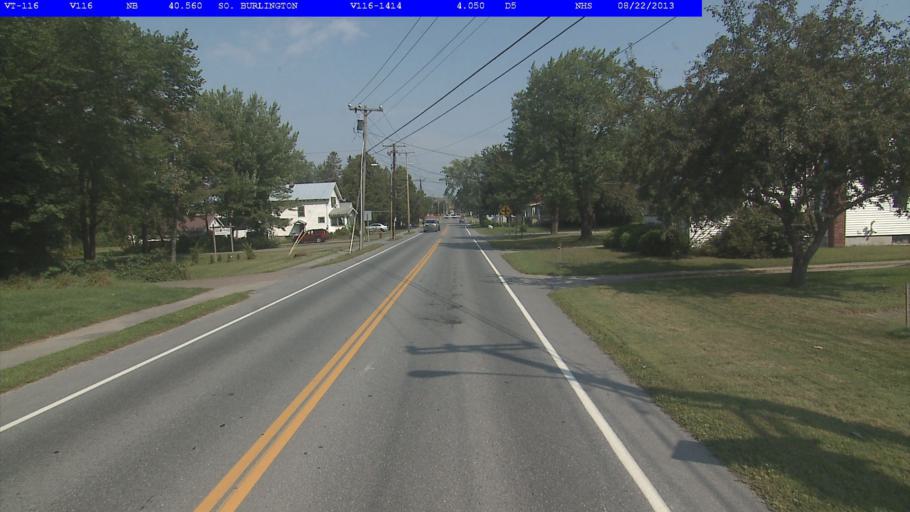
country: US
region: Vermont
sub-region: Chittenden County
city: South Burlington
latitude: 44.4643
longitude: -73.1708
